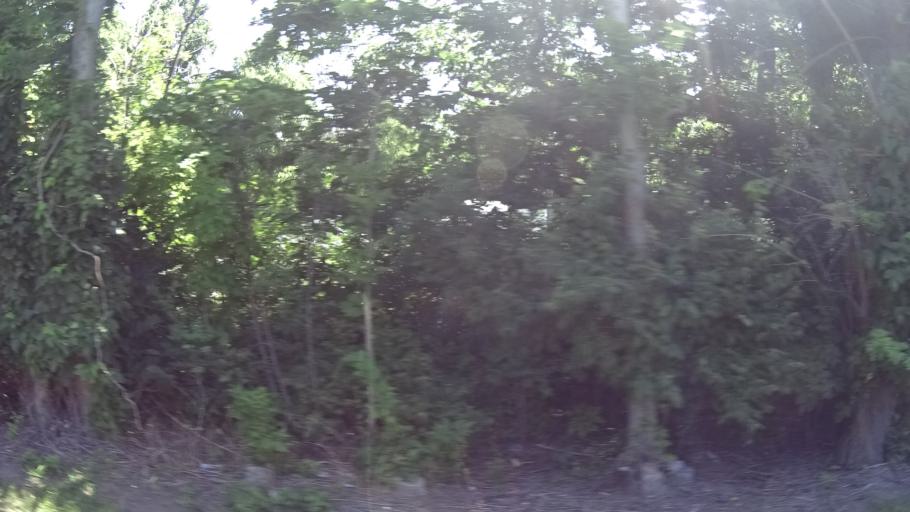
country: US
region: Ohio
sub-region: Ottawa County
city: Port Clinton
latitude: 41.4395
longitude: -82.8430
